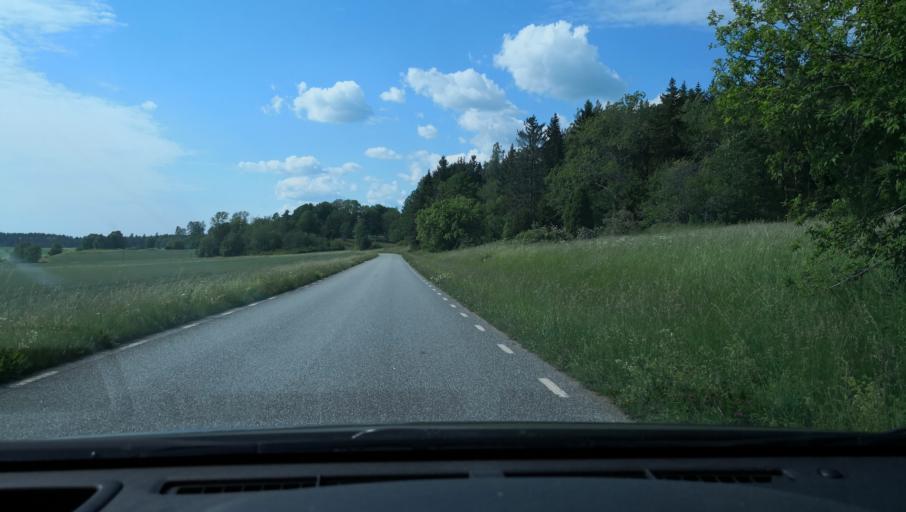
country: SE
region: Uppsala
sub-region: Enkopings Kommun
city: Orsundsbro
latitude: 59.8333
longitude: 17.3157
